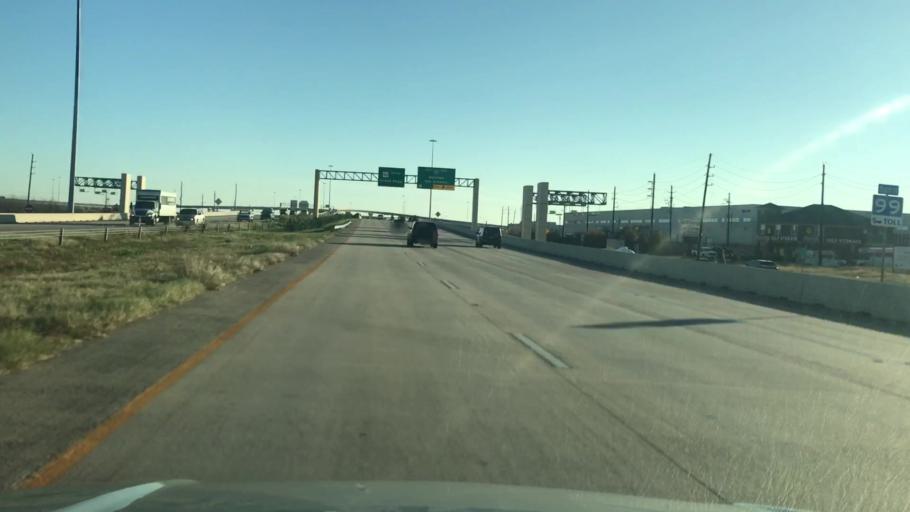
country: US
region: Texas
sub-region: Harris County
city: Katy
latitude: 29.7972
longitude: -95.7762
